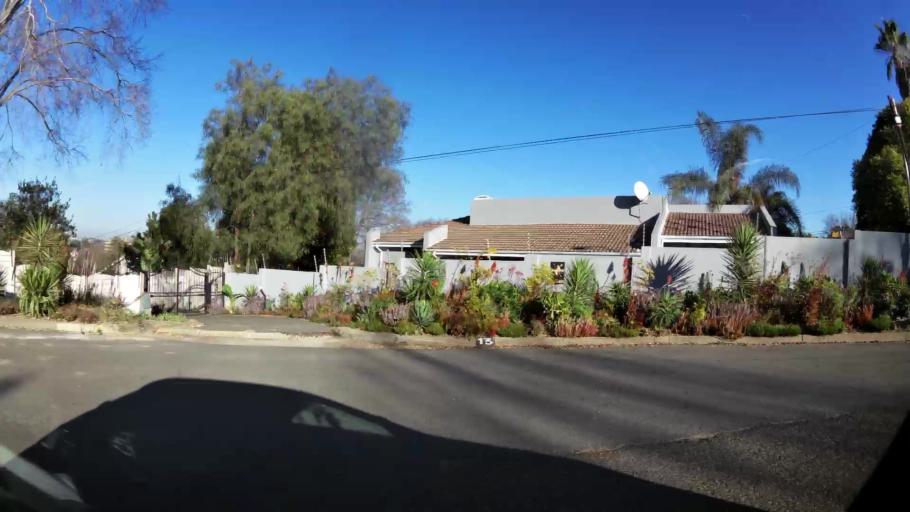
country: ZA
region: Gauteng
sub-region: City of Johannesburg Metropolitan Municipality
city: Midrand
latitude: -26.0346
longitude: 28.0725
